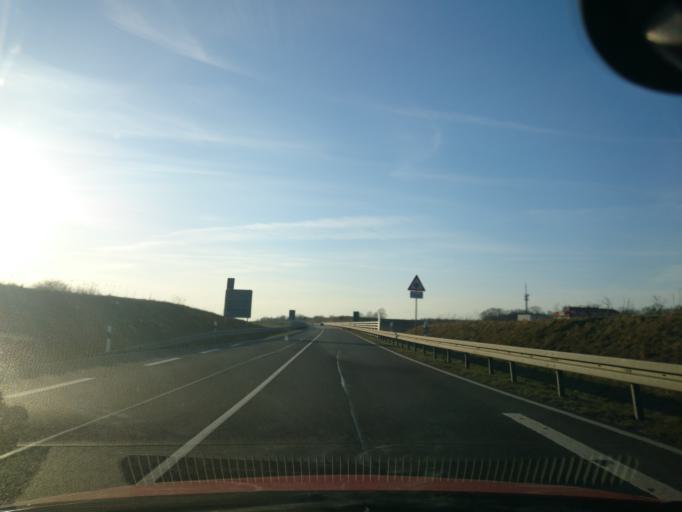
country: DE
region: Mecklenburg-Vorpommern
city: Stralsund
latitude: 54.2954
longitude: 13.0485
